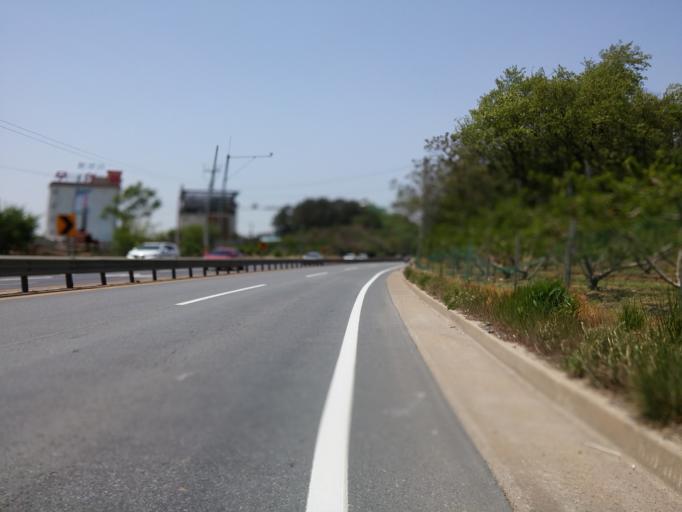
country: KR
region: Chungcheongnam-do
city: Nonsan
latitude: 36.2115
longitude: 127.1545
